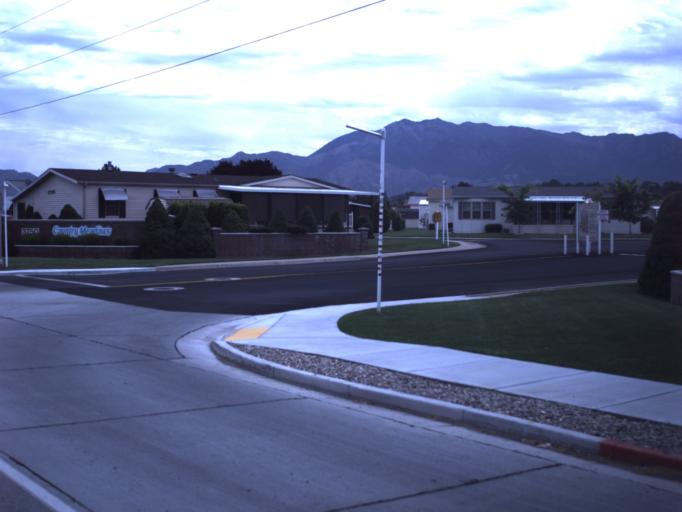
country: US
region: Utah
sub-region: Weber County
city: West Haven
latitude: 41.1954
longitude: -112.0430
